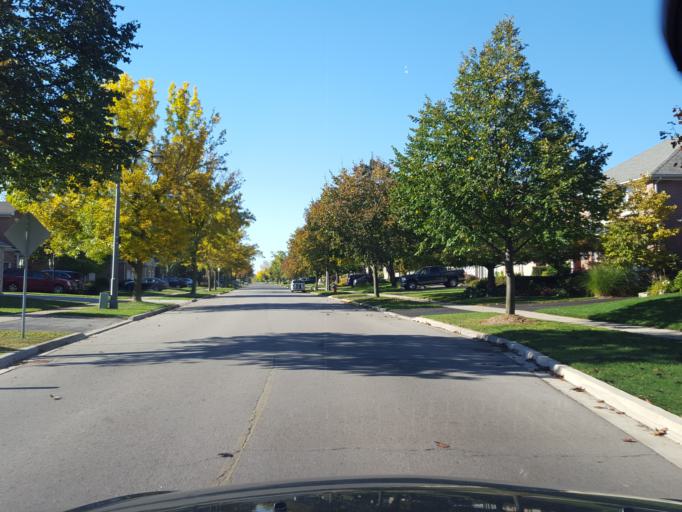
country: CA
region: Ontario
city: Burlington
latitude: 43.3879
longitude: -79.8038
